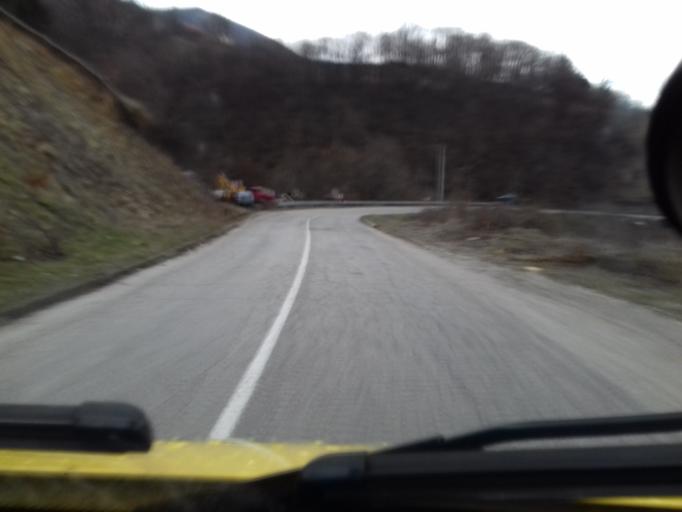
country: BA
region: Federation of Bosnia and Herzegovina
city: Turbe
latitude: 44.2614
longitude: 17.5460
